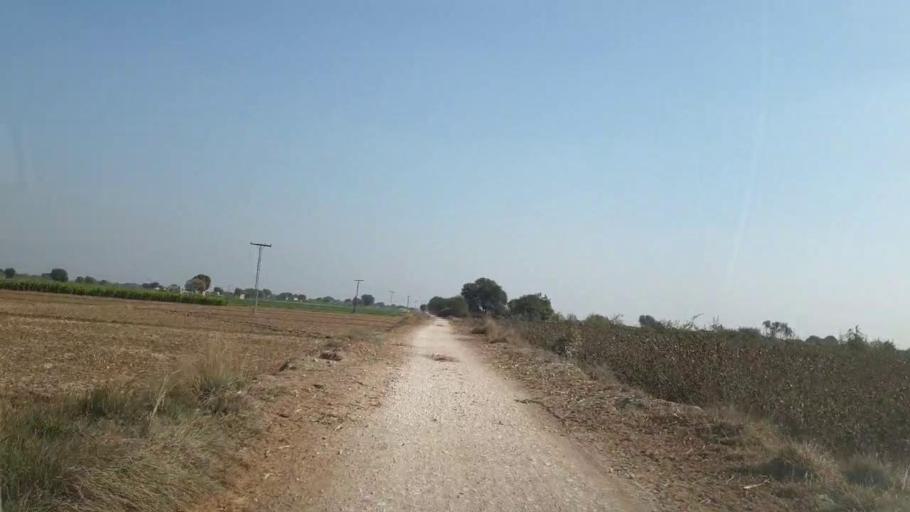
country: PK
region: Sindh
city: Tando Jam
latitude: 25.5087
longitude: 68.4887
